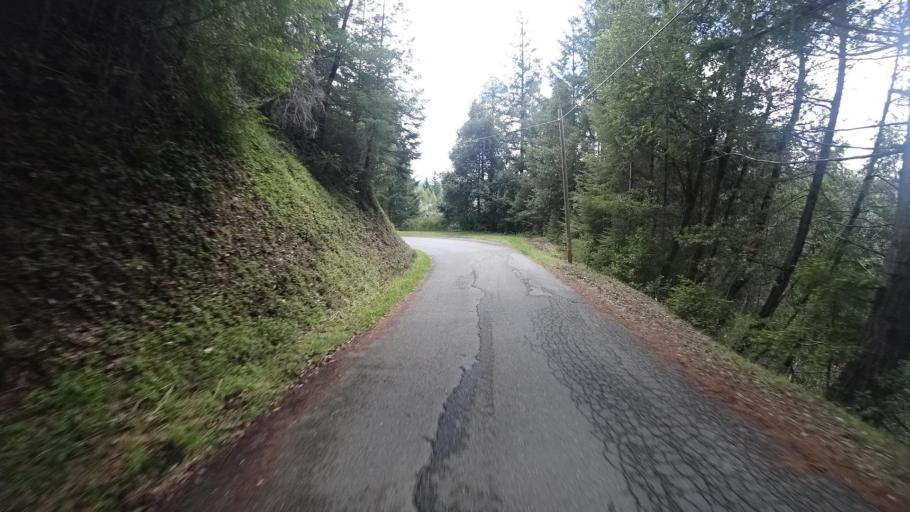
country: US
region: California
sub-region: Humboldt County
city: Blue Lake
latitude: 40.7654
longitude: -123.9286
